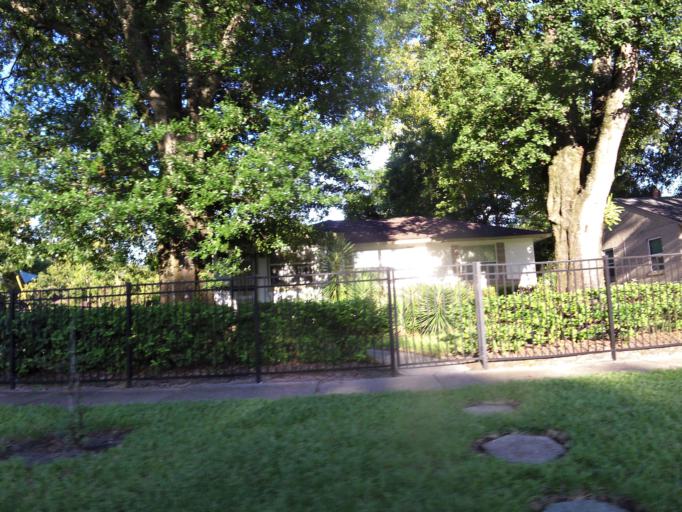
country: US
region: Florida
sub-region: Duval County
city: Jacksonville
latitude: 30.3609
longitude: -81.7006
